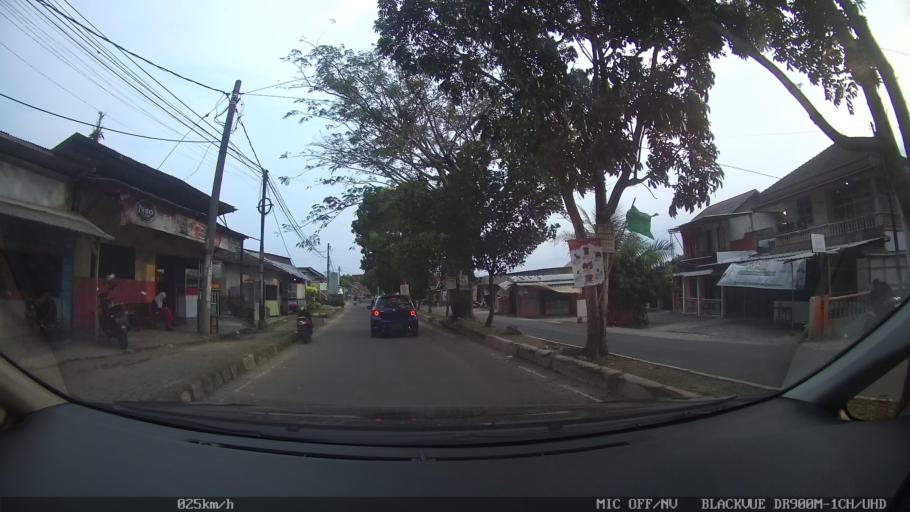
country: ID
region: Lampung
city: Kedaton
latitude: -5.3615
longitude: 105.2350
